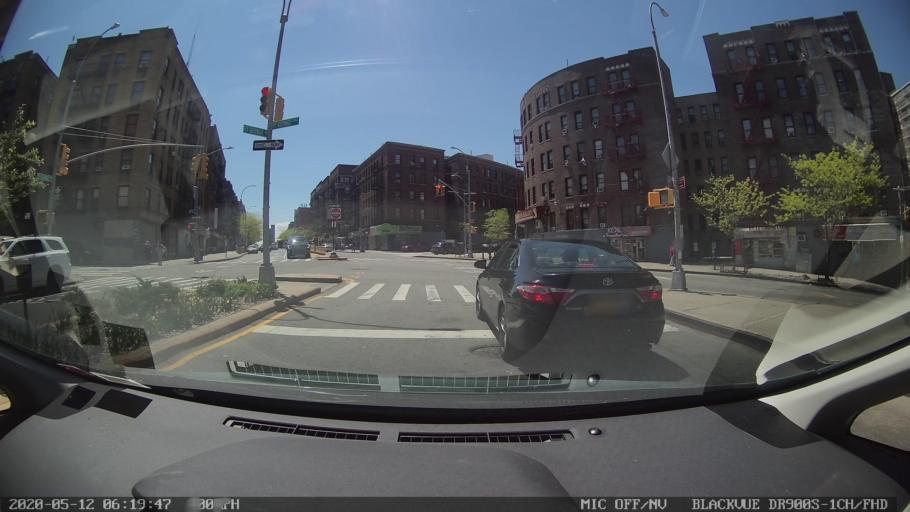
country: US
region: New York
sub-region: New York County
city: Inwood
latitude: 40.8570
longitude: -73.9280
